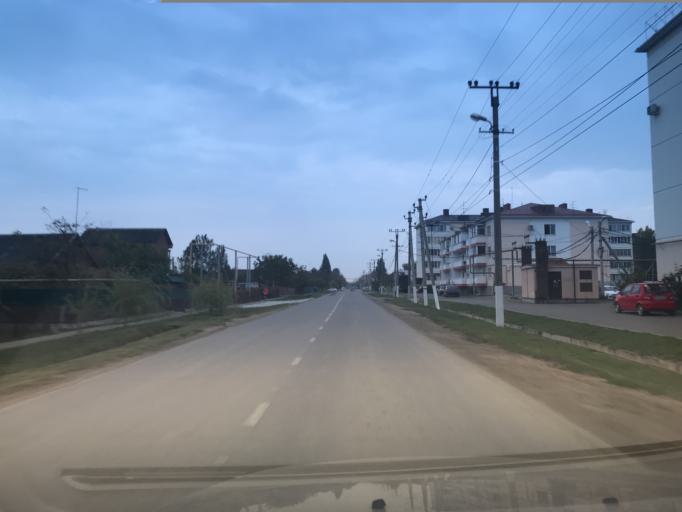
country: RU
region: Krasnodarskiy
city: Sovkhoznyy
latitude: 45.2709
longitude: 38.1045
